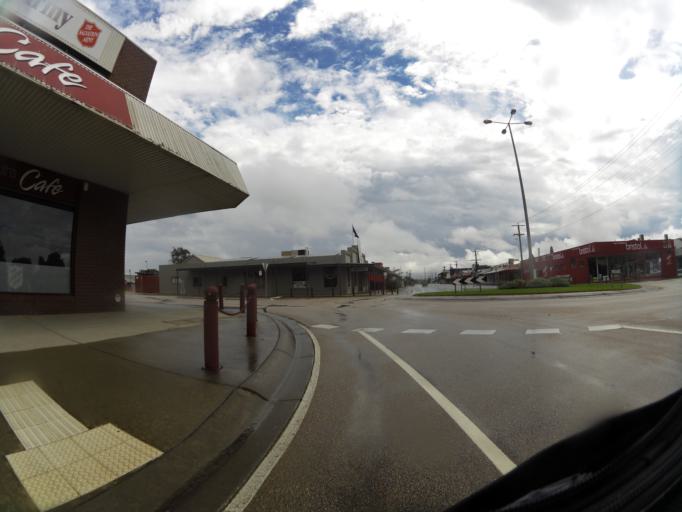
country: AU
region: Victoria
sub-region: East Gippsland
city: Bairnsdale
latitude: -37.8271
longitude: 147.6327
